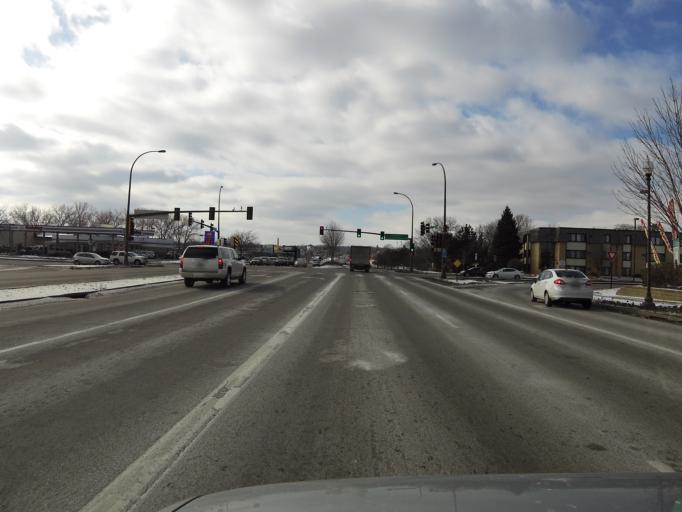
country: US
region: Minnesota
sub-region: Hennepin County
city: Minnetonka Mills
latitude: 44.9209
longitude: -93.4133
